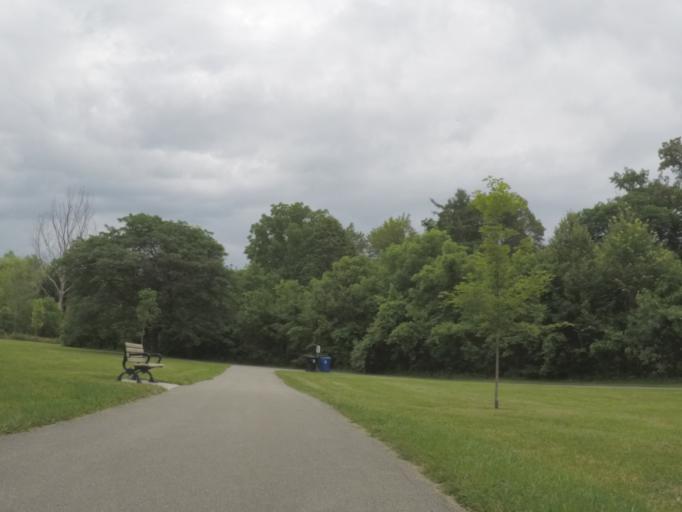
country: CA
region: Ontario
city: Etobicoke
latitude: 43.6559
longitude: -79.5518
